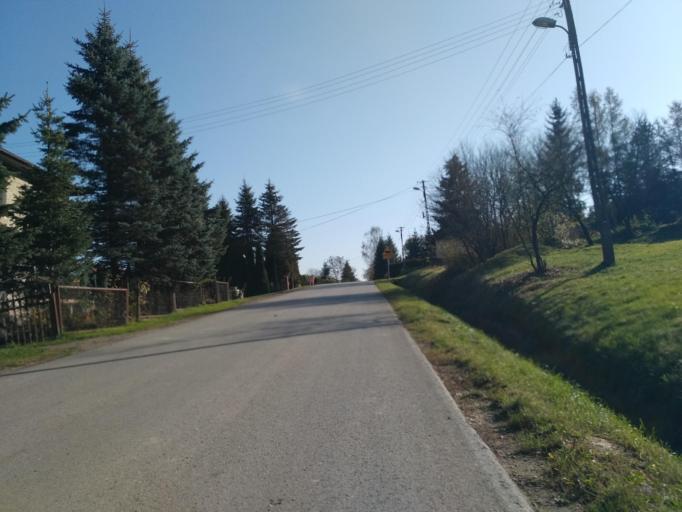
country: PL
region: Subcarpathian Voivodeship
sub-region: Powiat brzozowski
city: Nozdrzec
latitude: 49.8036
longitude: 22.1688
